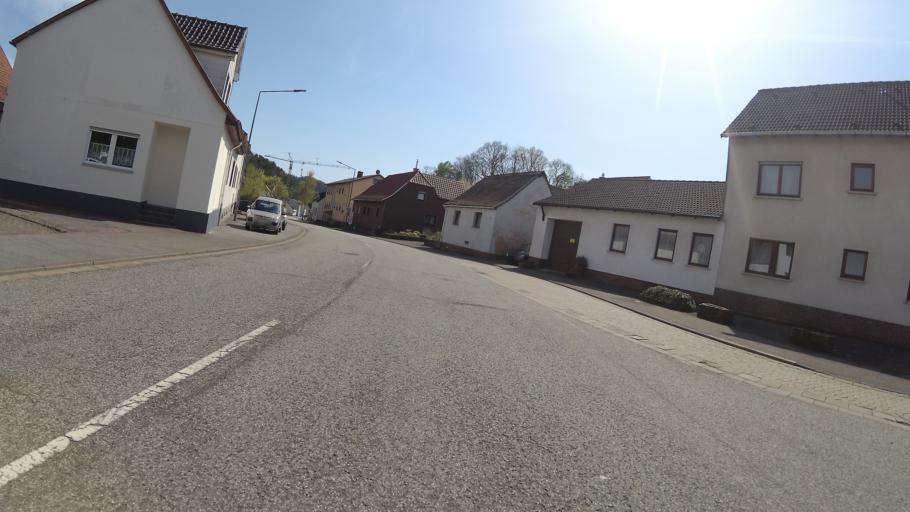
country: DE
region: Saarland
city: Homburg
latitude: 49.3397
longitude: 7.3686
